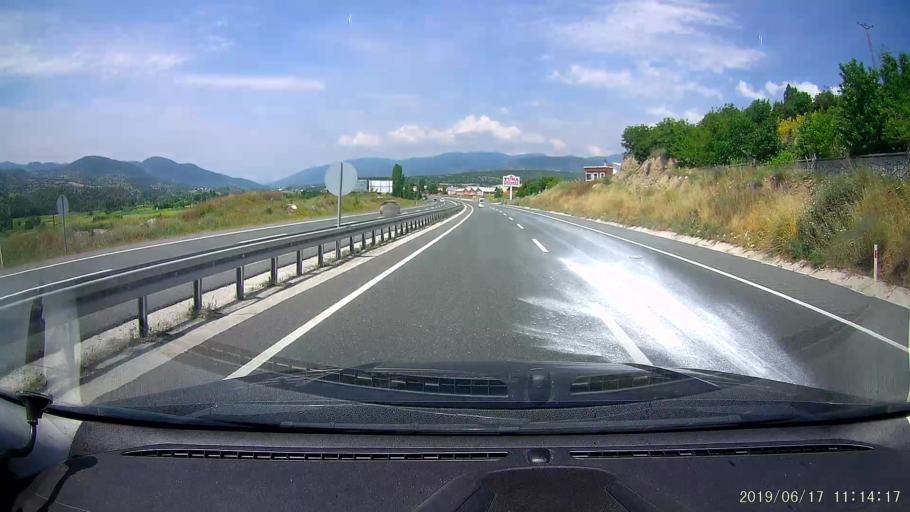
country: TR
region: Kastamonu
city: Tosya
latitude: 40.9575
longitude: 33.9519
